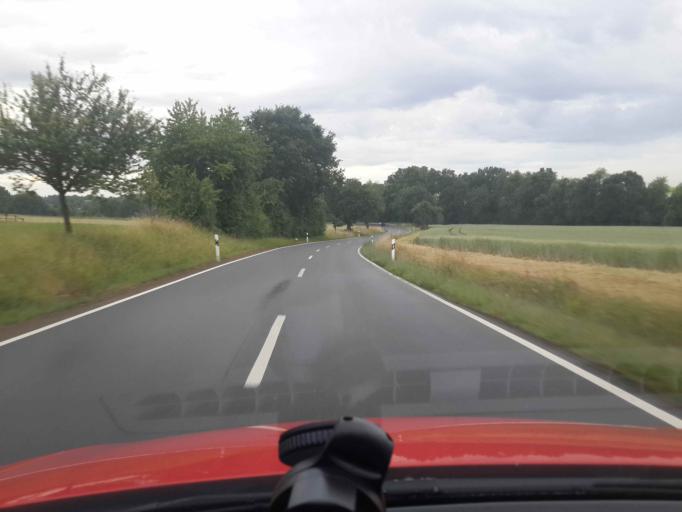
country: DE
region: Baden-Wuerttemberg
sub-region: Karlsruhe Region
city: Limbach
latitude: 49.4312
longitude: 9.2004
